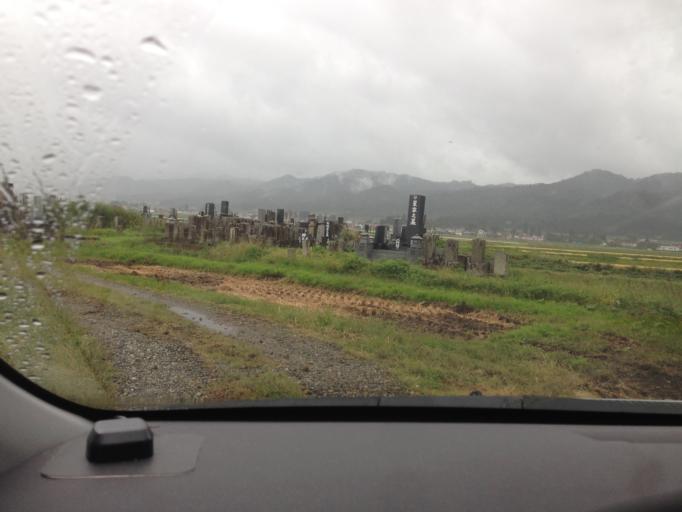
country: JP
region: Fukushima
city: Kitakata
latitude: 37.4751
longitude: 139.8292
